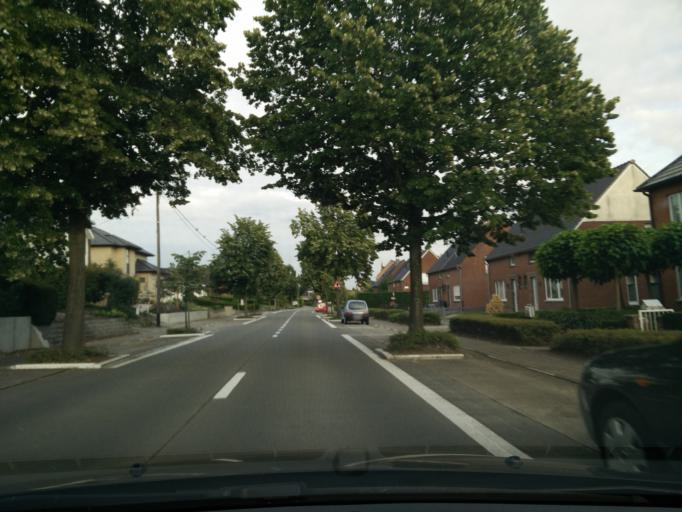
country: BE
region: Flanders
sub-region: Provincie Antwerpen
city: Bornem
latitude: 51.0928
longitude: 4.2481
